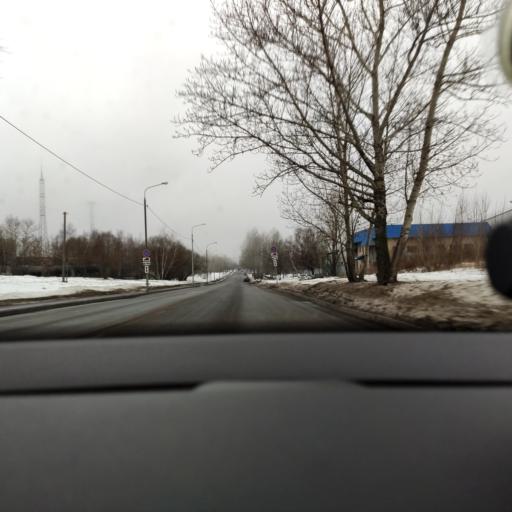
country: RU
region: Moskovskaya
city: Biryulevo Zapadnoye
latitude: 55.5813
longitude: 37.6313
